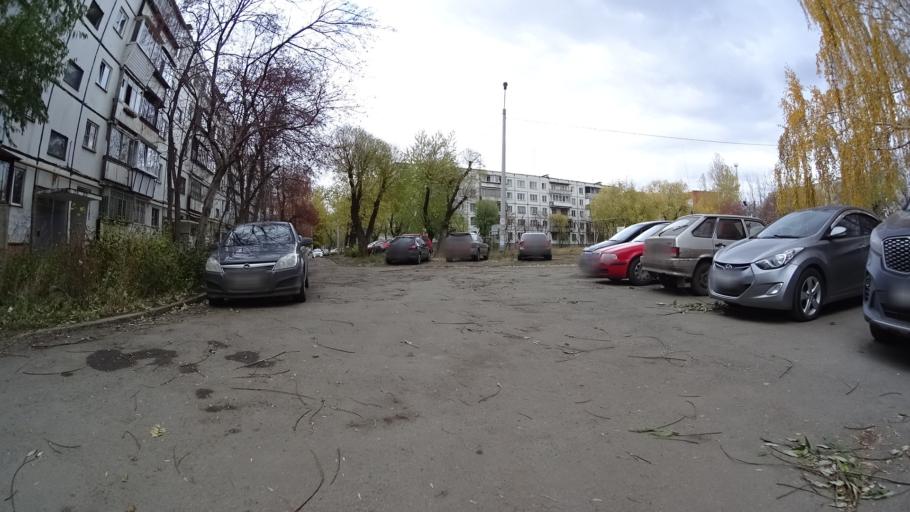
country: RU
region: Chelyabinsk
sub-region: Gorod Chelyabinsk
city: Chelyabinsk
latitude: 55.1894
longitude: 61.3077
